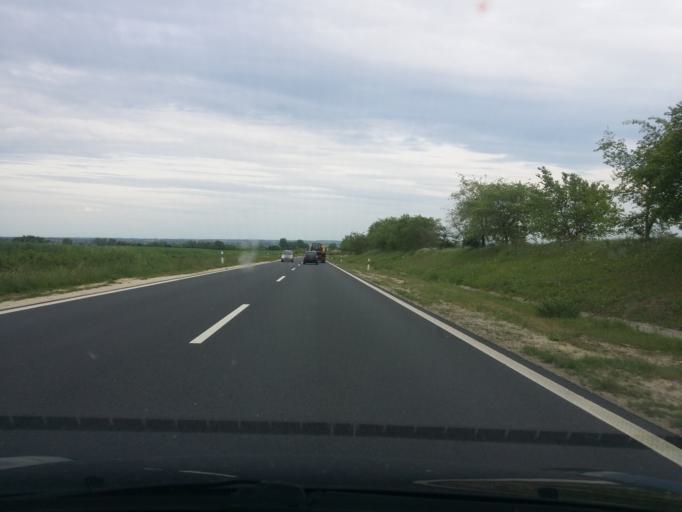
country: HU
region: Veszprem
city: Balatonkenese
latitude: 47.0313
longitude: 18.1702
